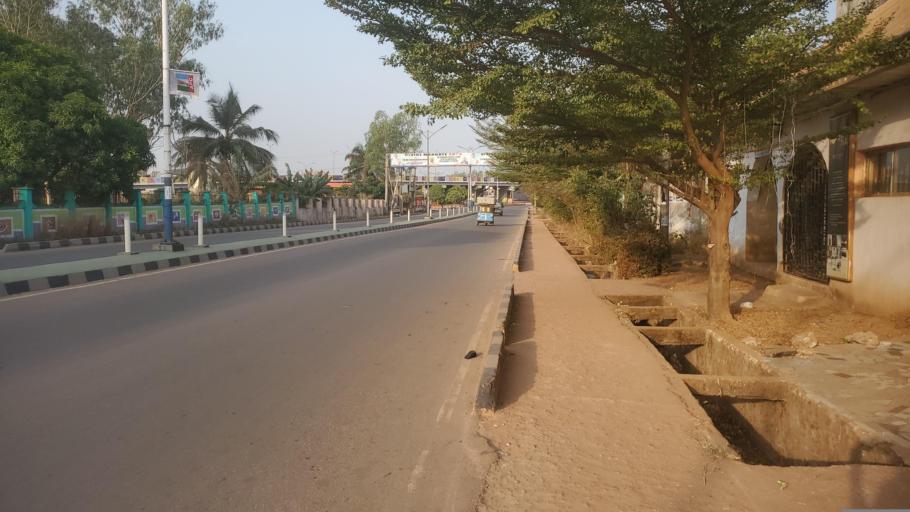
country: NG
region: Ebonyi
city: Abakaliki
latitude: 6.3258
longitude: 8.0860
